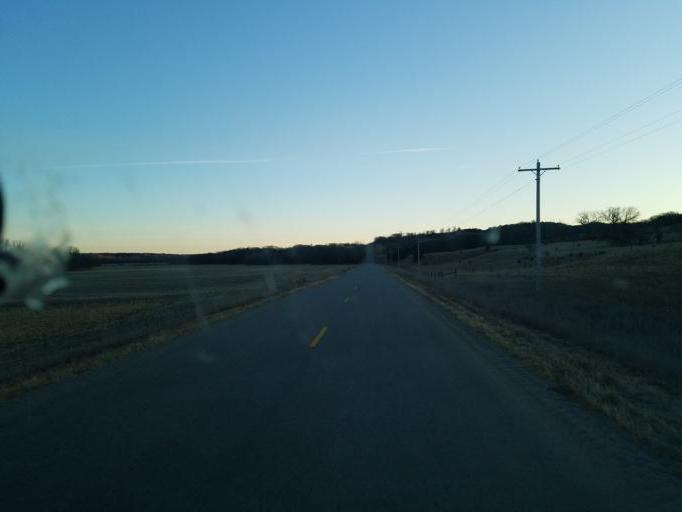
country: US
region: Nebraska
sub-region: Knox County
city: Center
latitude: 42.6485
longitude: -97.8874
